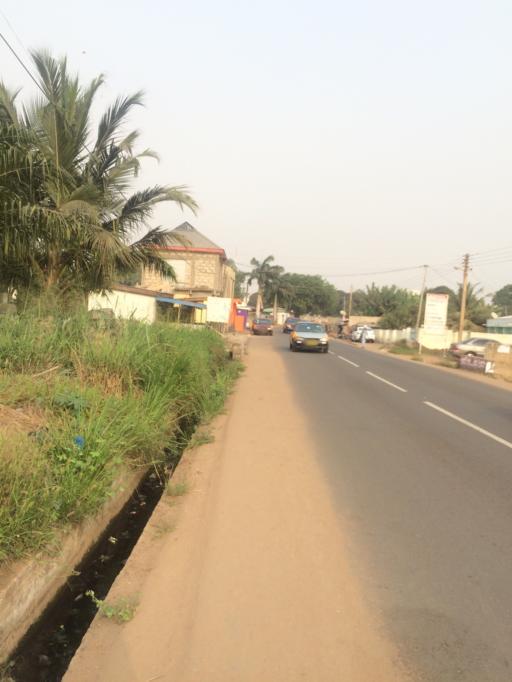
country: GH
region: Greater Accra
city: Nungua
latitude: 5.6042
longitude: -0.0826
